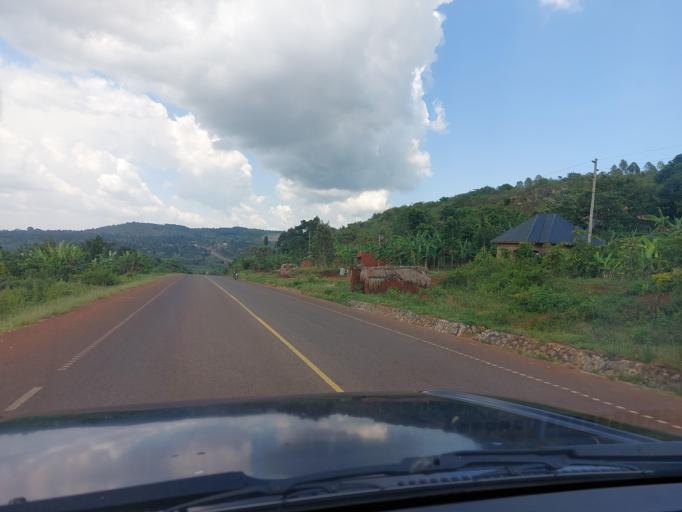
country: UG
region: Central Region
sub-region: Buikwe District
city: Njeru
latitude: 0.3355
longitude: 33.1233
